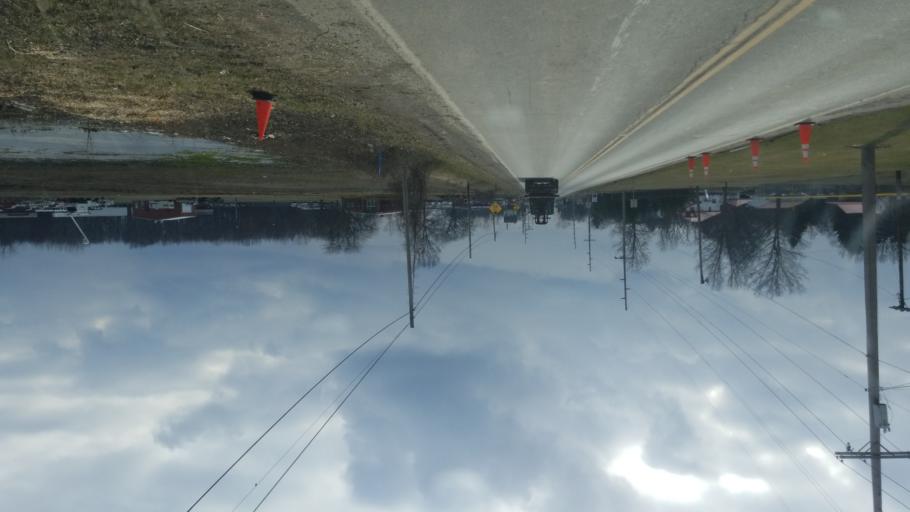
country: US
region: Ohio
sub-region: Marion County
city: Marion
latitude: 40.6019
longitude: -83.0702
